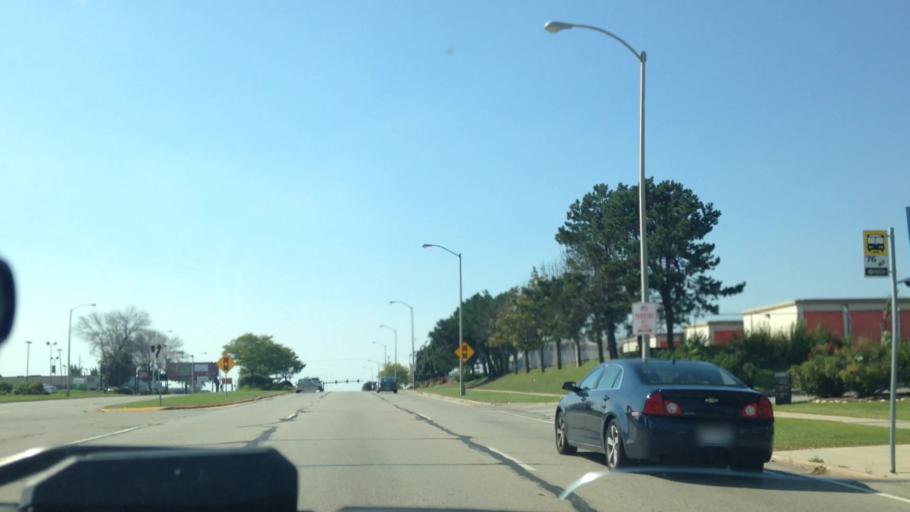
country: US
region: Wisconsin
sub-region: Milwaukee County
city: Brown Deer
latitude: 43.1778
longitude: -88.0203
